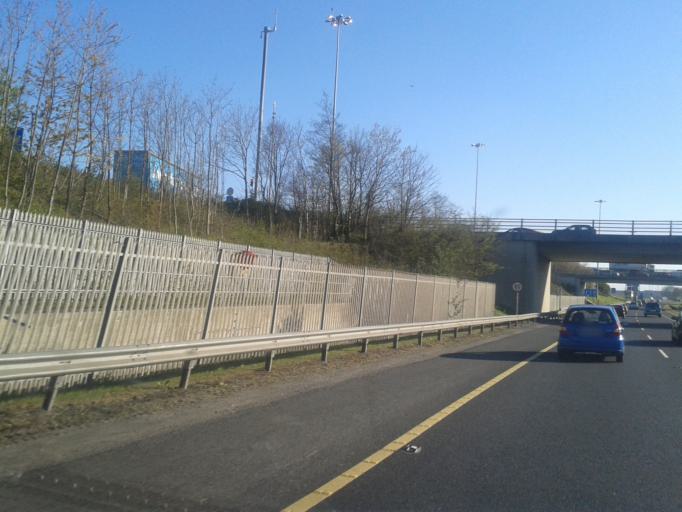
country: IE
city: Bonnybrook
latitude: 53.4115
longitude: -6.2257
